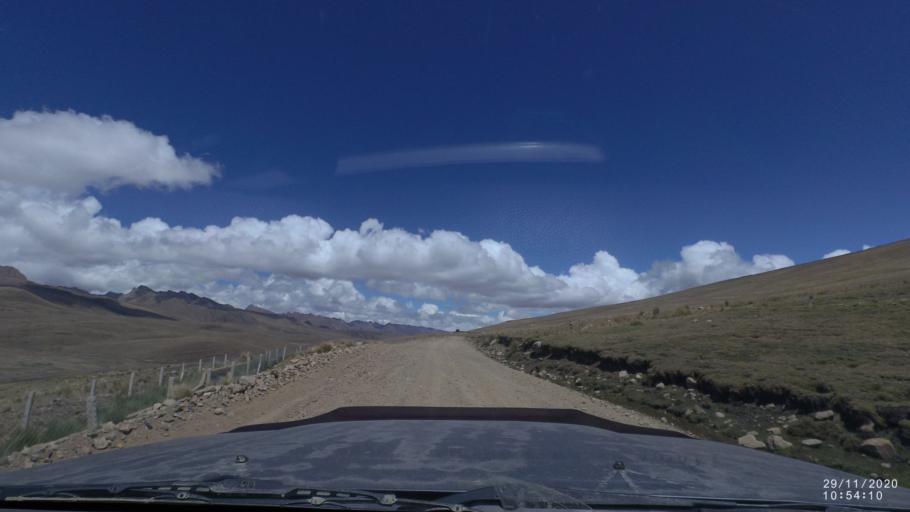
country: BO
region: Cochabamba
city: Cochabamba
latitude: -17.2298
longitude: -66.2182
